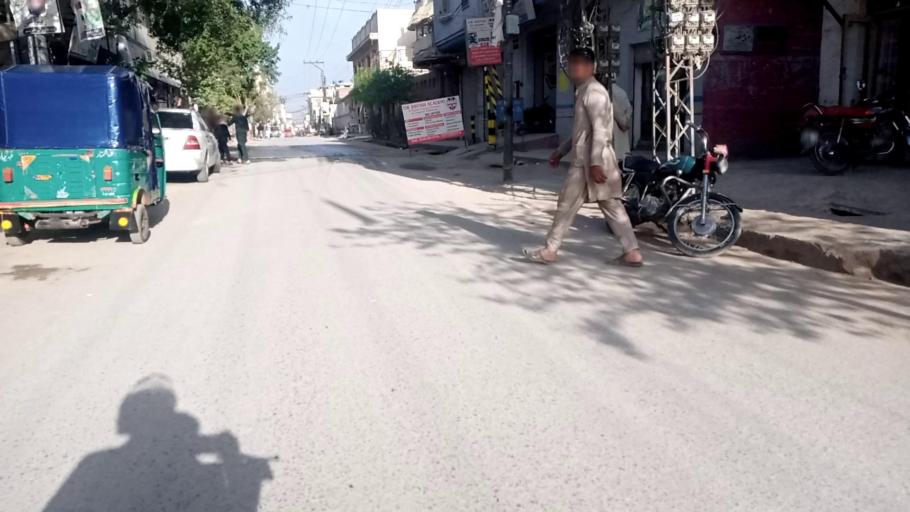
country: PK
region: Khyber Pakhtunkhwa
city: Peshawar
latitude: 34.0102
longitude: 71.5992
